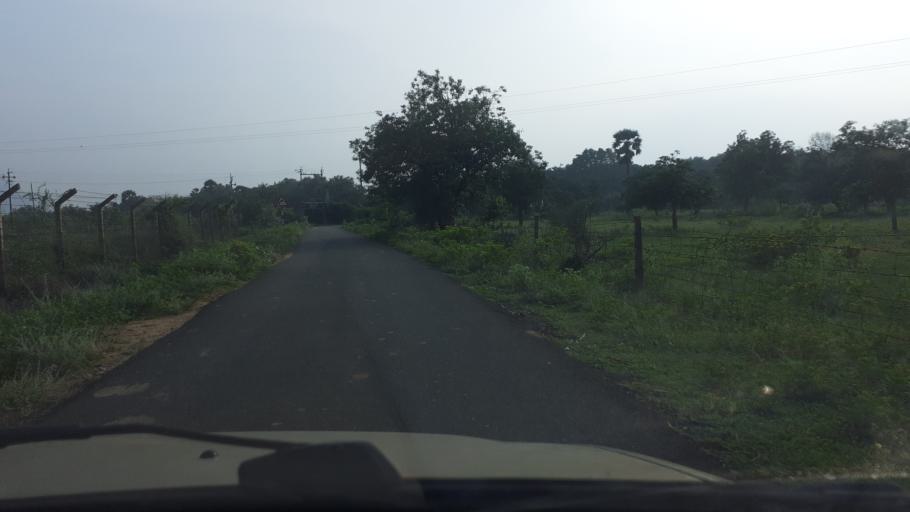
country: IN
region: Tamil Nadu
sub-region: Tirunelveli Kattabo
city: Kalakkadu
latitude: 8.4689
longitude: 77.5850
